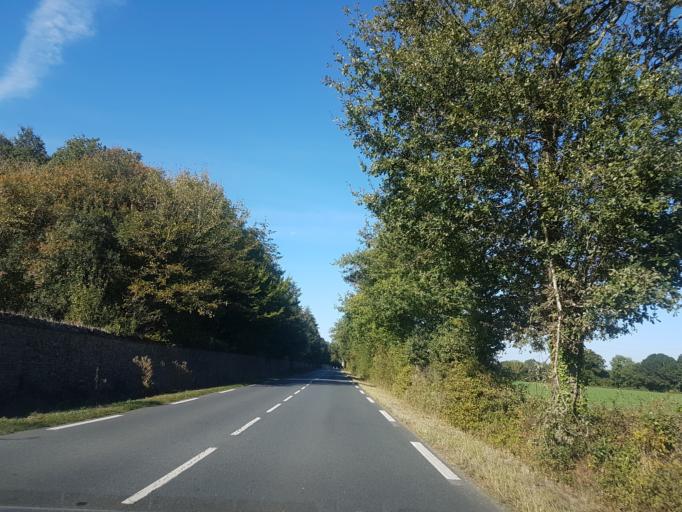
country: FR
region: Pays de la Loire
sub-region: Departement de la Loire-Atlantique
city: Nort-sur-Erdre
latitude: 47.4172
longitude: -1.4778
